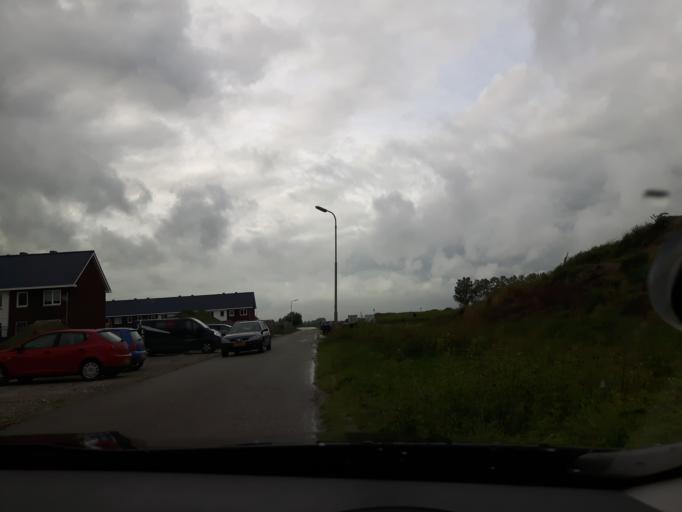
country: NL
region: Zeeland
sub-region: Gemeente Goes
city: Goes
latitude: 51.5182
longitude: 3.8963
